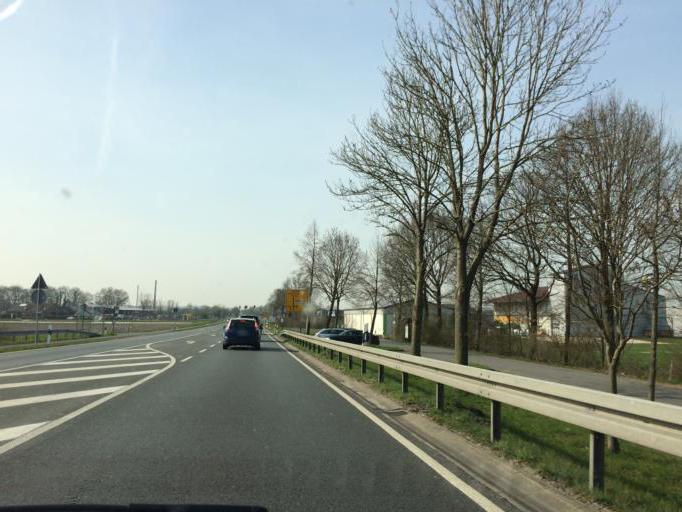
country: DE
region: North Rhine-Westphalia
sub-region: Regierungsbezirk Munster
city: Nottuln
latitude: 51.9085
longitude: 7.4021
